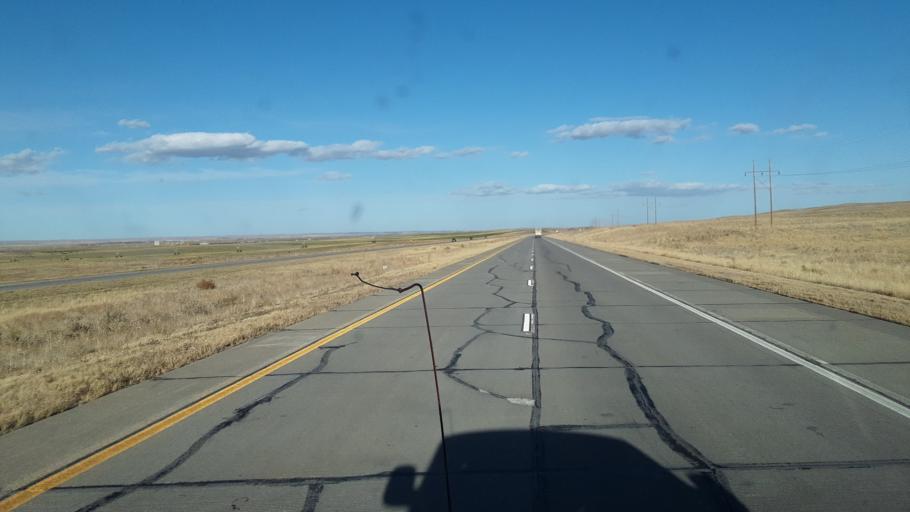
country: US
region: Colorado
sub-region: Logan County
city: Sterling
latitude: 40.7495
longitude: -102.9855
